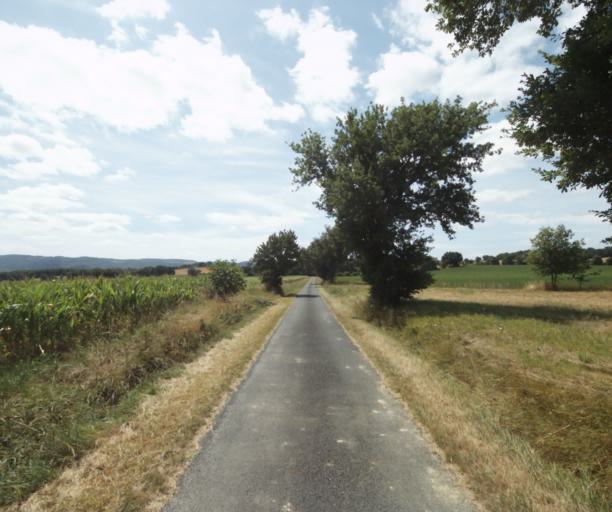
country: FR
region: Midi-Pyrenees
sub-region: Departement du Tarn
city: Soreze
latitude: 43.5009
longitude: 2.0655
